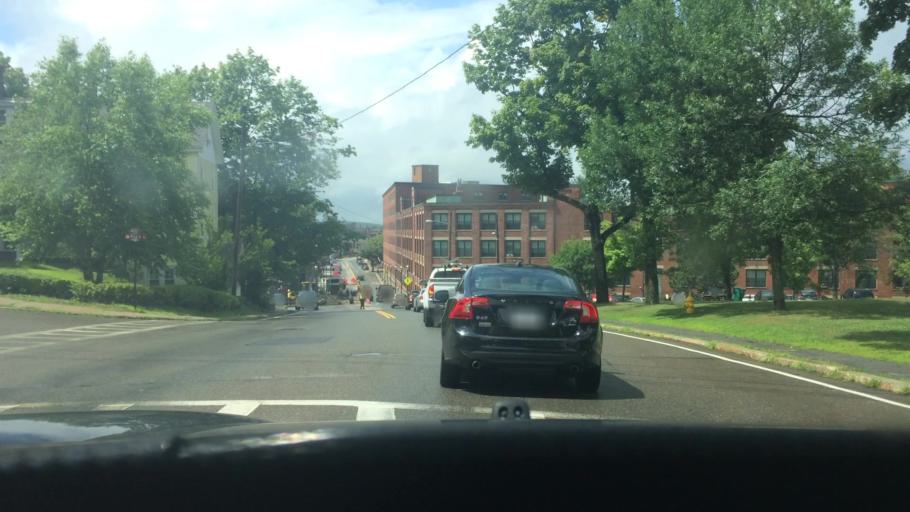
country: US
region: Massachusetts
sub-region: Worcester County
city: Gardner
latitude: 42.5786
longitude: -71.9919
